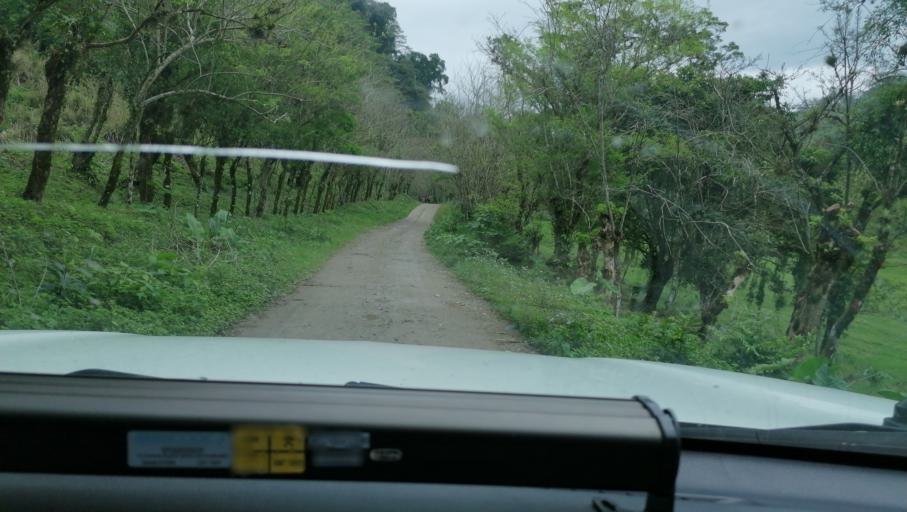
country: MX
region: Chiapas
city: Ixtacomitan
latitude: 17.3526
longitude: -93.1500
